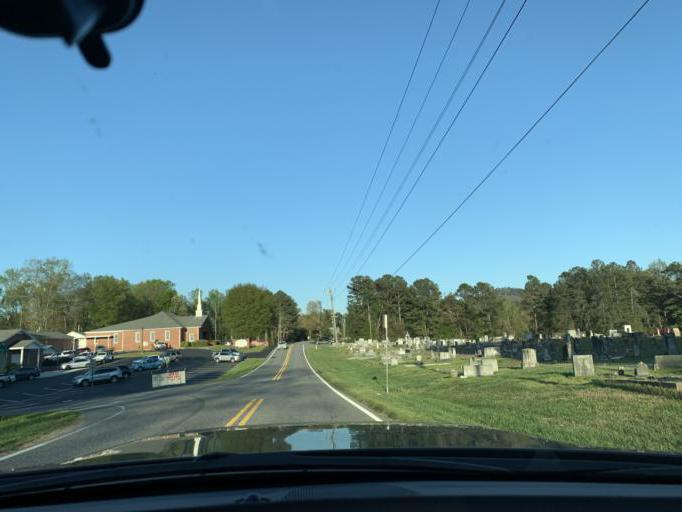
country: US
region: Georgia
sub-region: Forsyth County
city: Cumming
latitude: 34.2440
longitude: -84.1881
